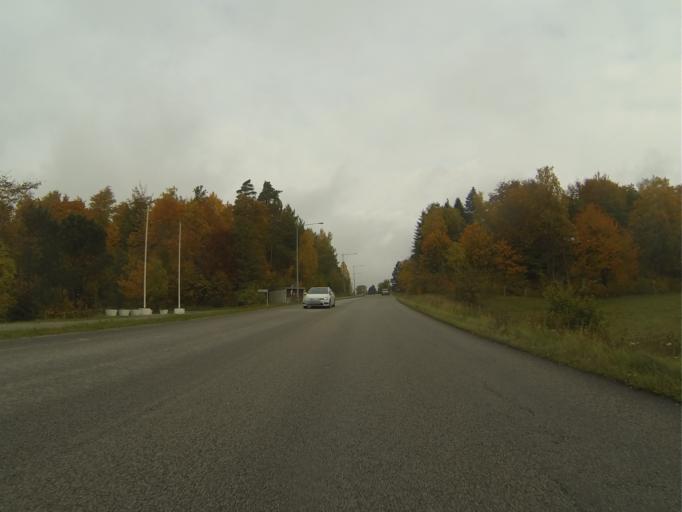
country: SE
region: Skane
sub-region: Sjobo Kommun
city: Sjoebo
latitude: 55.6244
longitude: 13.7048
